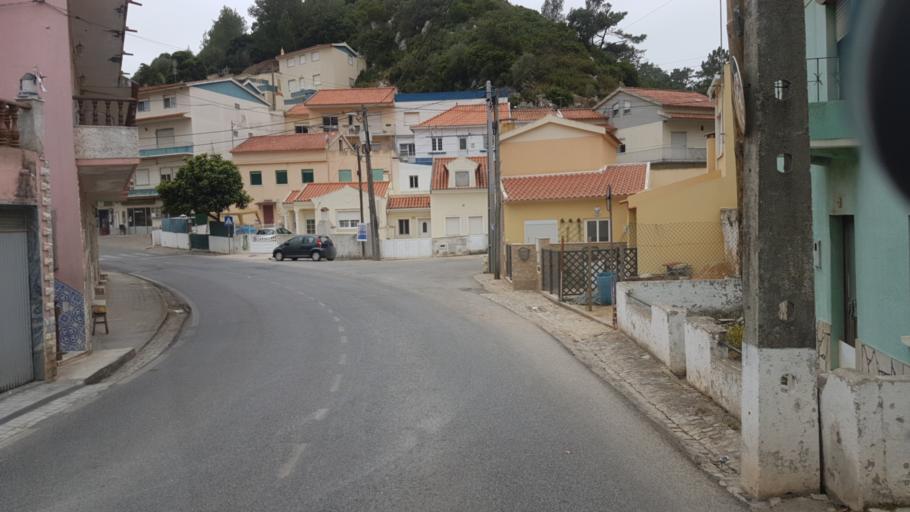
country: PT
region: Lisbon
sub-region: Torres Vedras
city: A dos Cunhados
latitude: 39.1823
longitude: -9.3306
